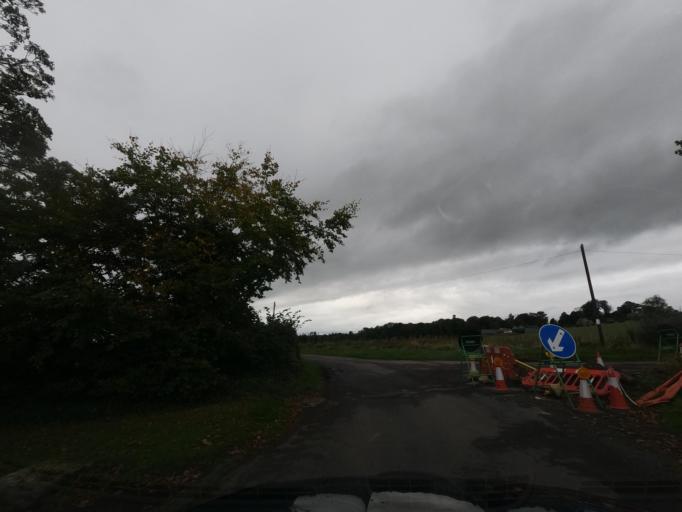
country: GB
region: England
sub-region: Northumberland
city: Ford
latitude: 55.6265
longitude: -2.0863
